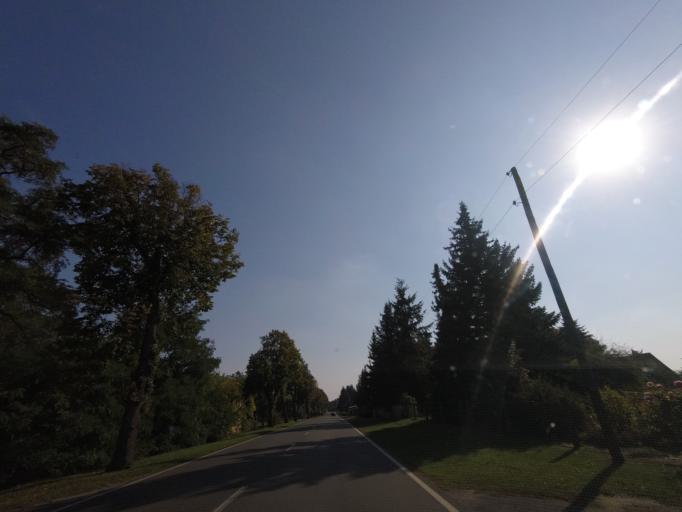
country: DE
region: Saxony-Anhalt
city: Jessen
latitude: 51.8011
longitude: 13.0168
